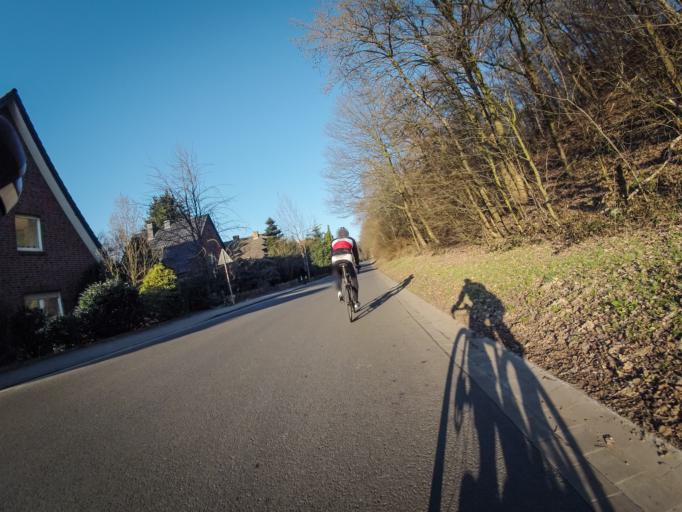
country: DE
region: Lower Saxony
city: Wallenhorst
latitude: 52.3202
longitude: 8.0036
